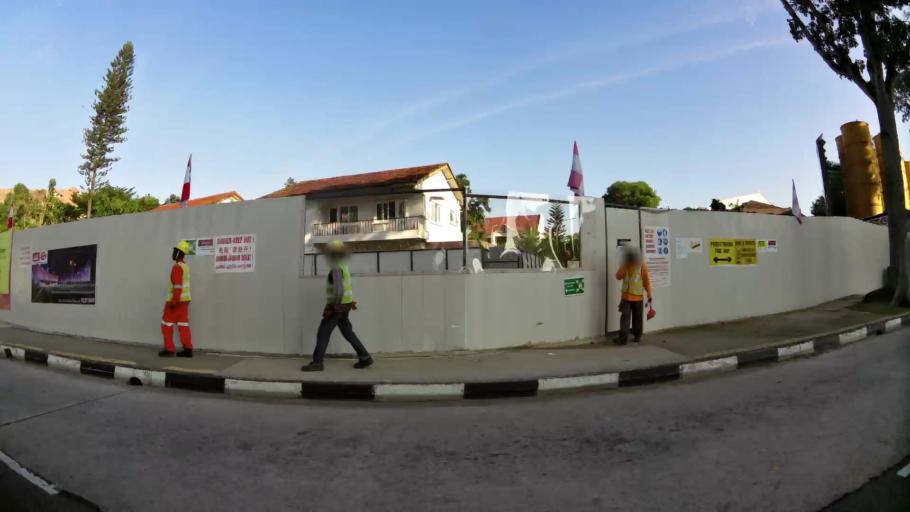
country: SG
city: Singapore
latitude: 1.3097
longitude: 103.9292
